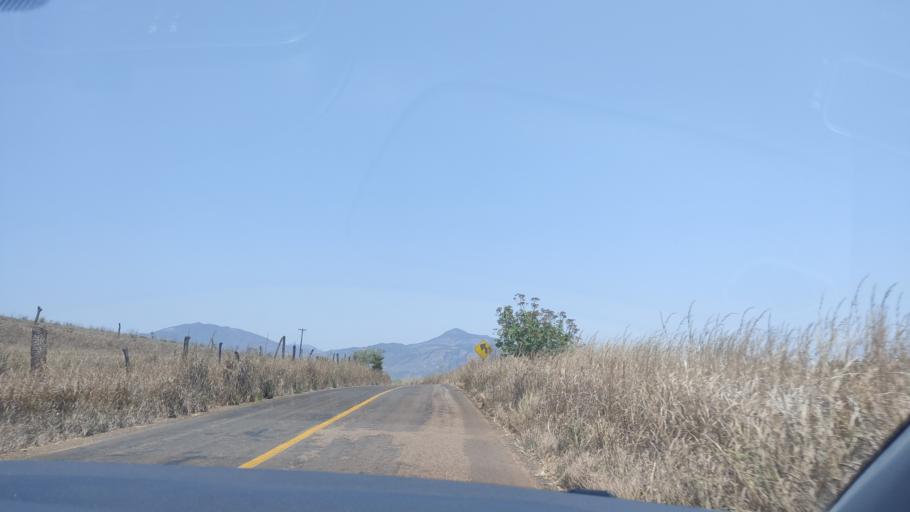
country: MX
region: Nayarit
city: Puga
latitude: 21.5764
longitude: -104.7552
